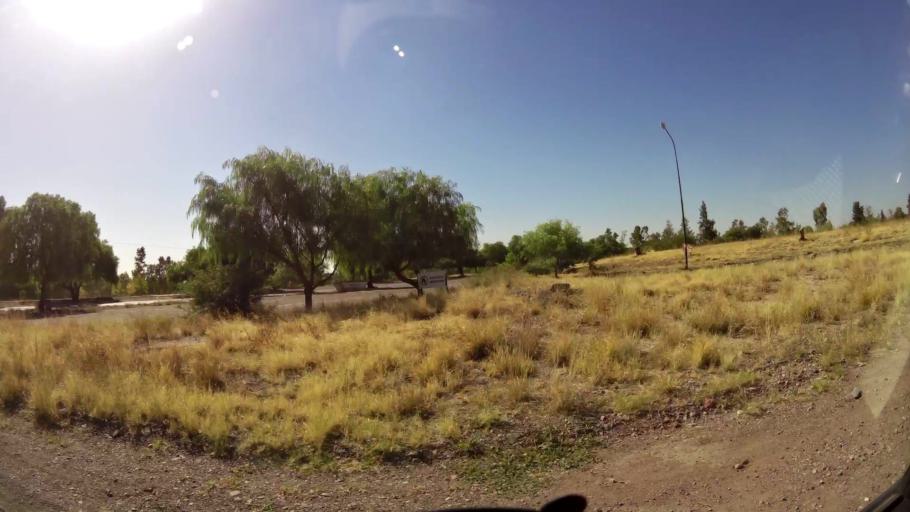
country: AR
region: Mendoza
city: Mendoza
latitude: -32.8957
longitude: -68.8823
